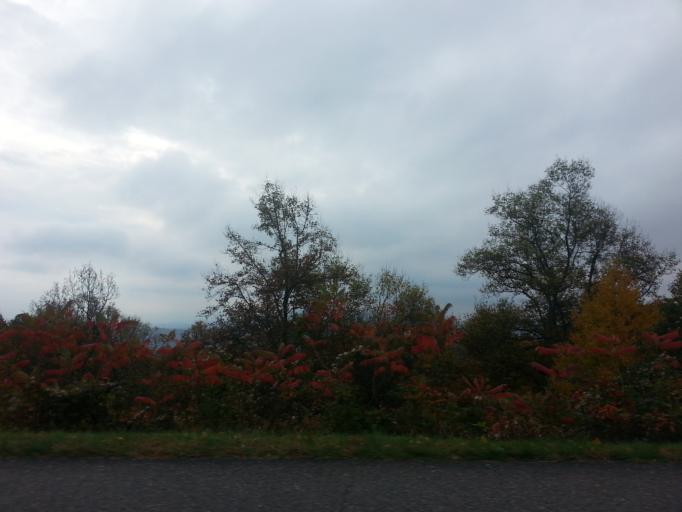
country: US
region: North Carolina
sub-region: Wilkes County
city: Millers Creek
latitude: 36.2770
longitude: -81.3802
